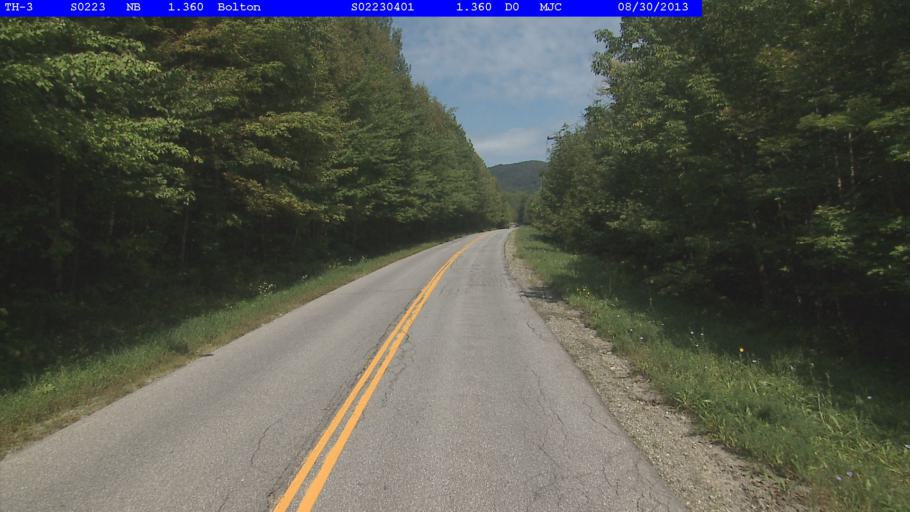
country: US
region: Vermont
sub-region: Washington County
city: Waterbury
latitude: 44.3898
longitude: -72.8752
